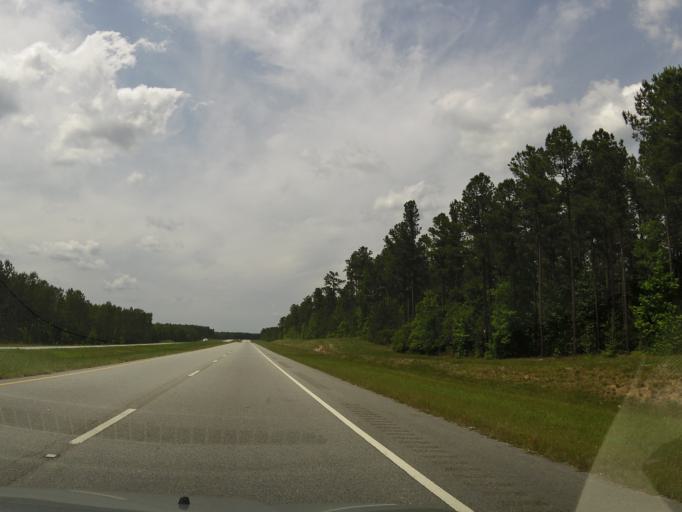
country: US
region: Georgia
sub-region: Jefferson County
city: Wadley
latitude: 32.7782
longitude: -82.3872
